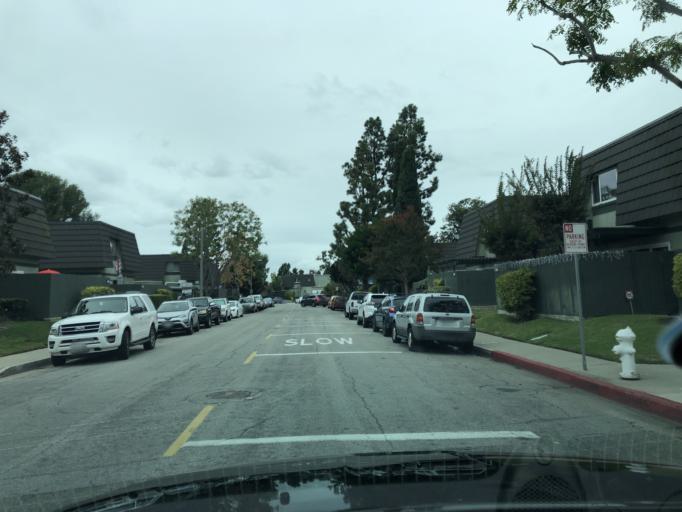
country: US
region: California
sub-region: Orange County
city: Fountain Valley
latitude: 33.6904
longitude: -117.9244
